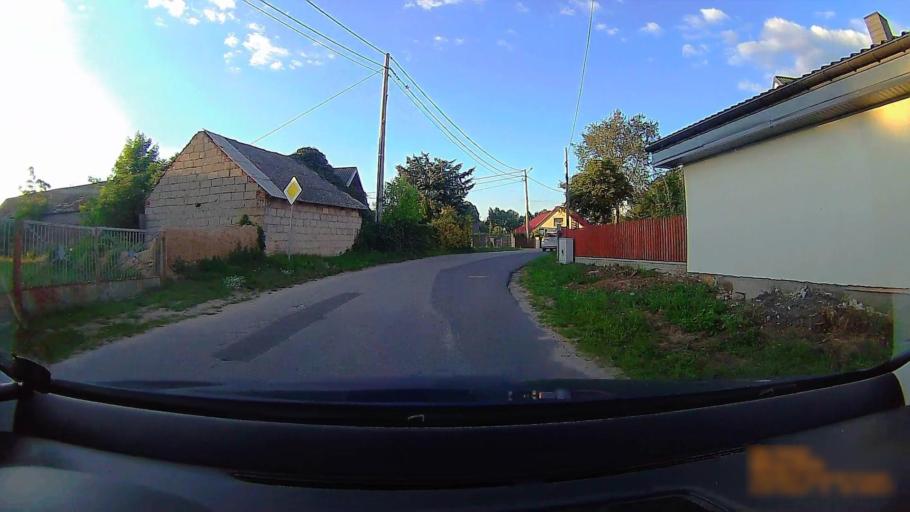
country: PL
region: Greater Poland Voivodeship
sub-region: Konin
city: Konin
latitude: 52.2156
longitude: 18.3260
